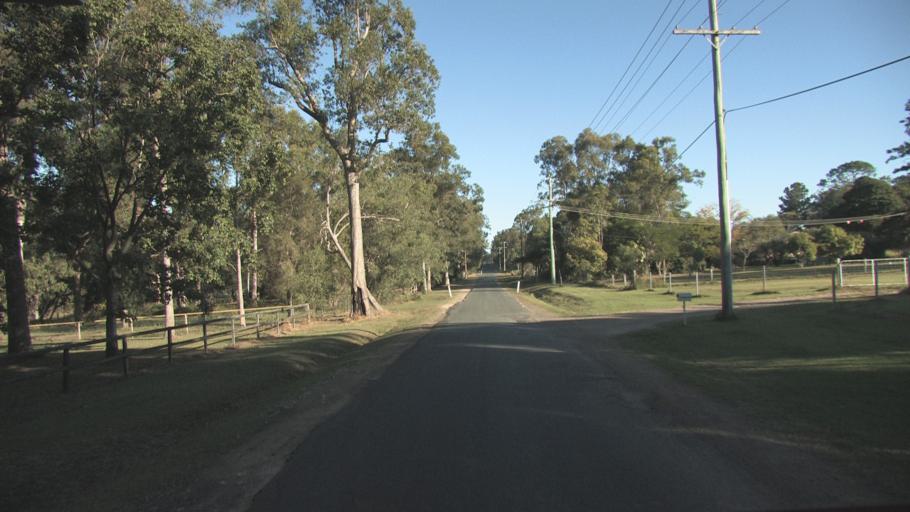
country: AU
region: Queensland
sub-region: Logan
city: Chambers Flat
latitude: -27.7812
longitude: 153.0872
